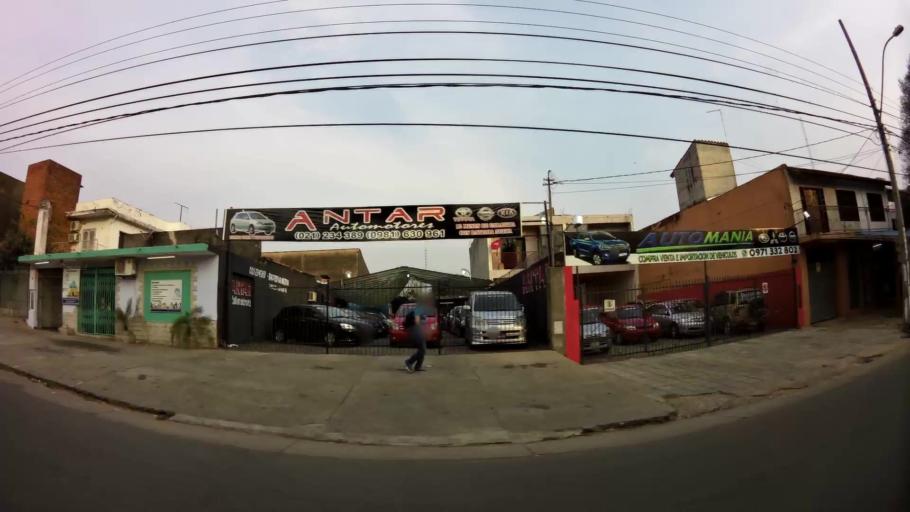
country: PY
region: Central
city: Lambare
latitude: -25.3287
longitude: -57.5850
